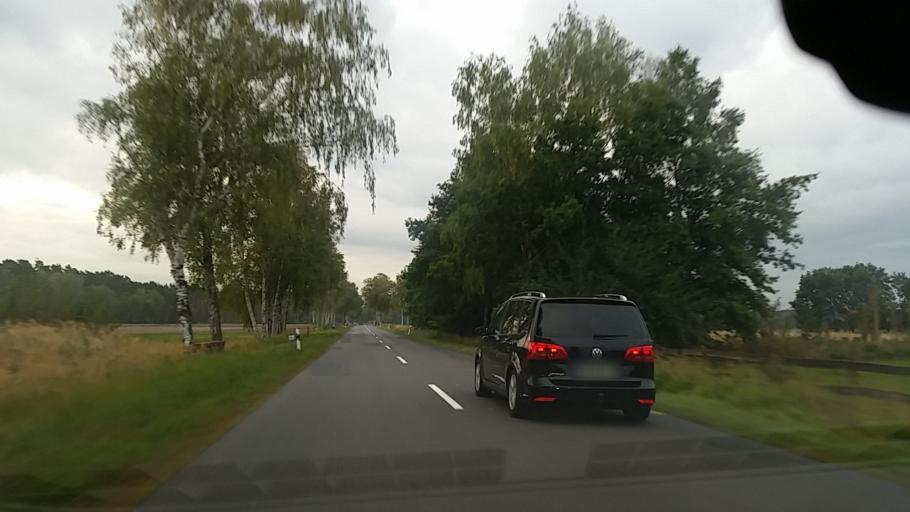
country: DE
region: Lower Saxony
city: Schoneworde
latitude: 52.6600
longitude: 10.6987
